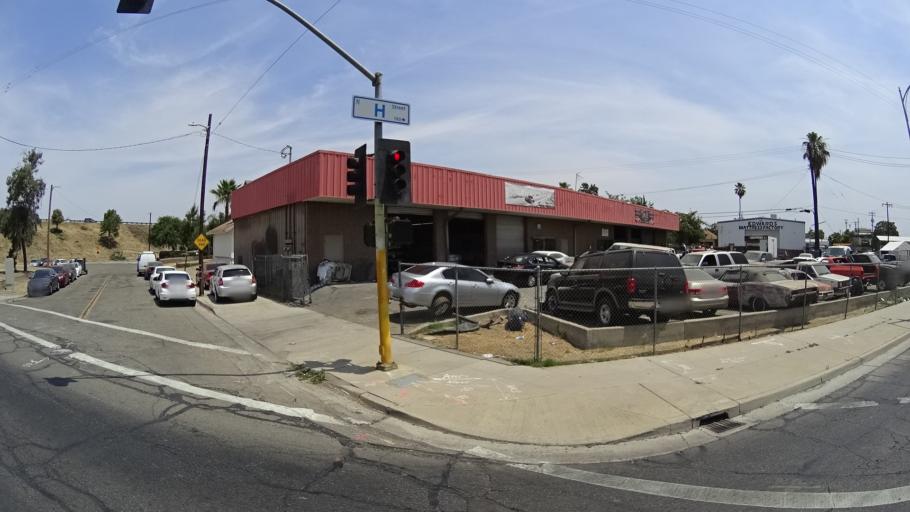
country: US
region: California
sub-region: Fresno County
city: Fresno
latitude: 36.7442
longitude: -119.8056
